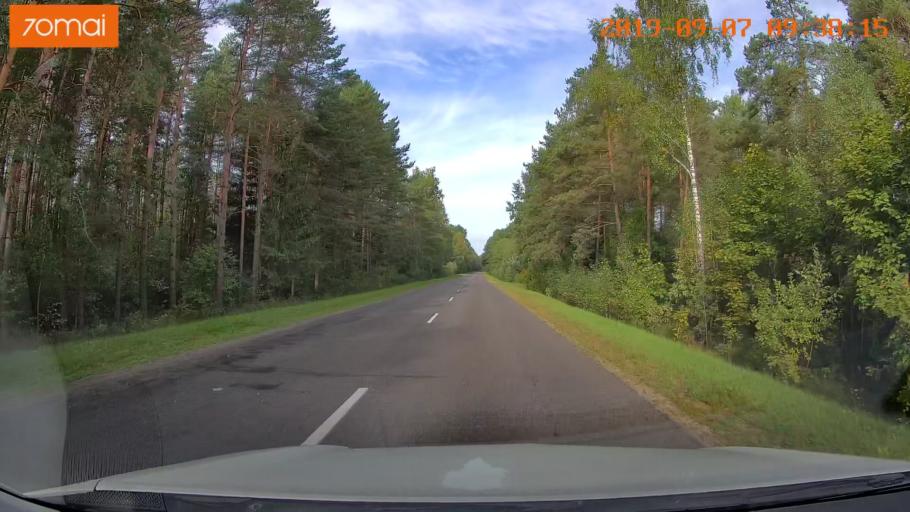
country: BY
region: Grodnenskaya
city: Iwye
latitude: 53.9234
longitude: 25.8255
